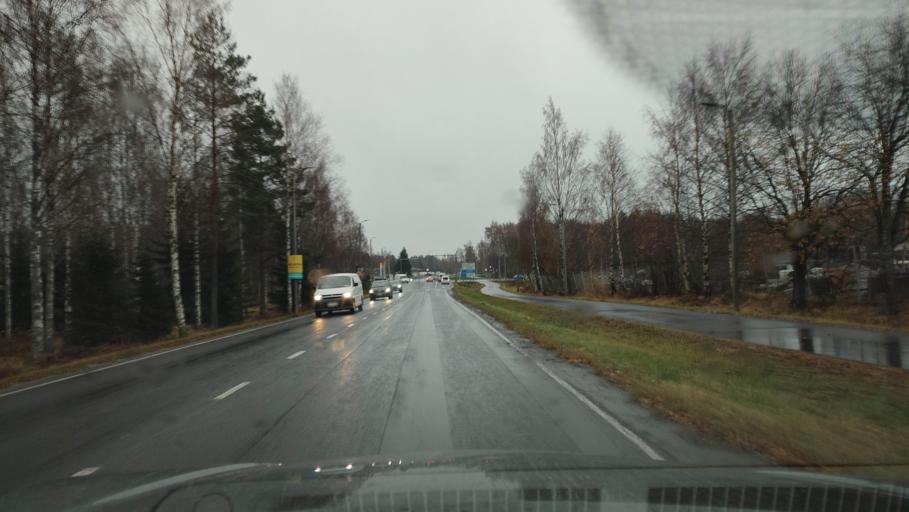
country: FI
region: Ostrobothnia
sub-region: Vaasa
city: Korsholm
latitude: 63.0915
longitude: 21.6537
